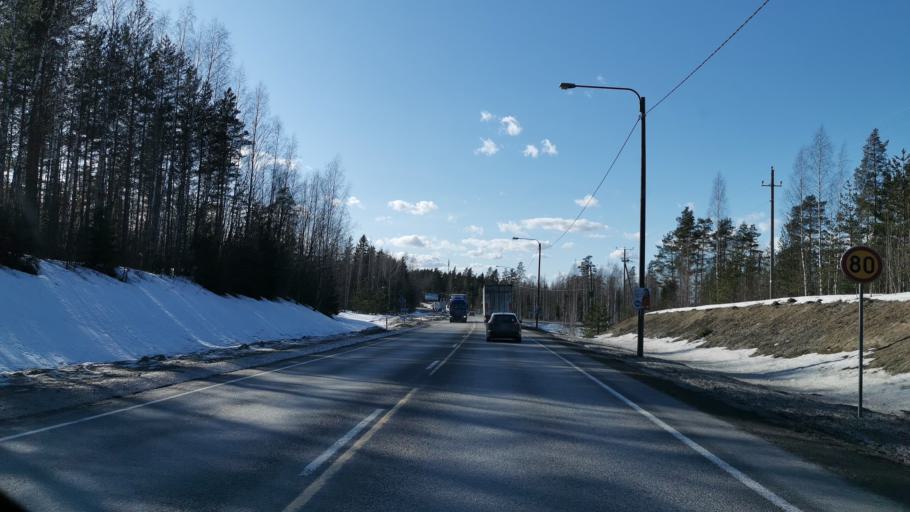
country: FI
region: Kymenlaakso
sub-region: Kouvola
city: Iitti
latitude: 60.8832
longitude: 26.4141
